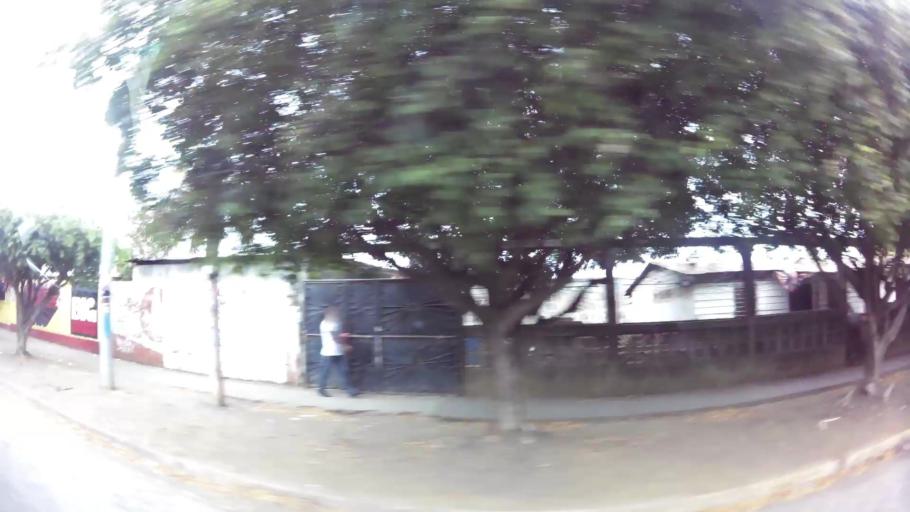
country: NI
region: Managua
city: Managua
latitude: 12.1170
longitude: -86.1987
